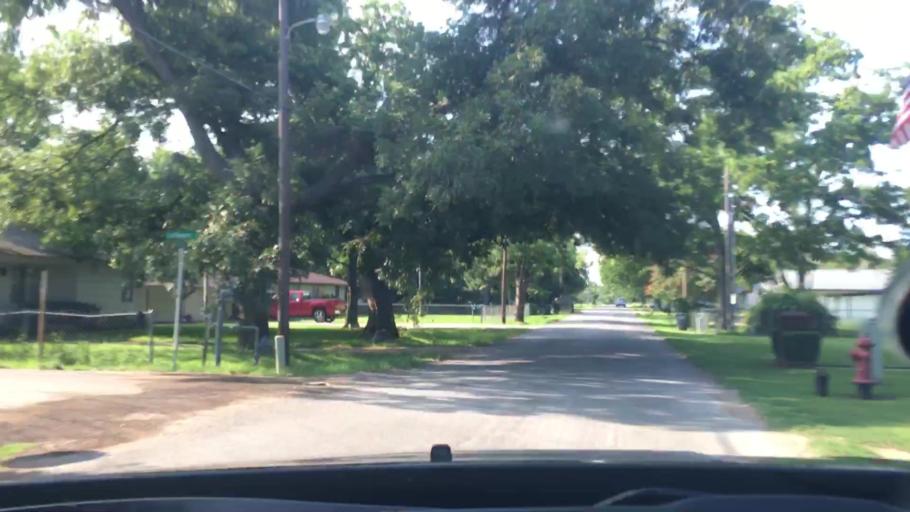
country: US
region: Oklahoma
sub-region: Johnston County
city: Tishomingo
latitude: 34.2292
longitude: -96.6711
